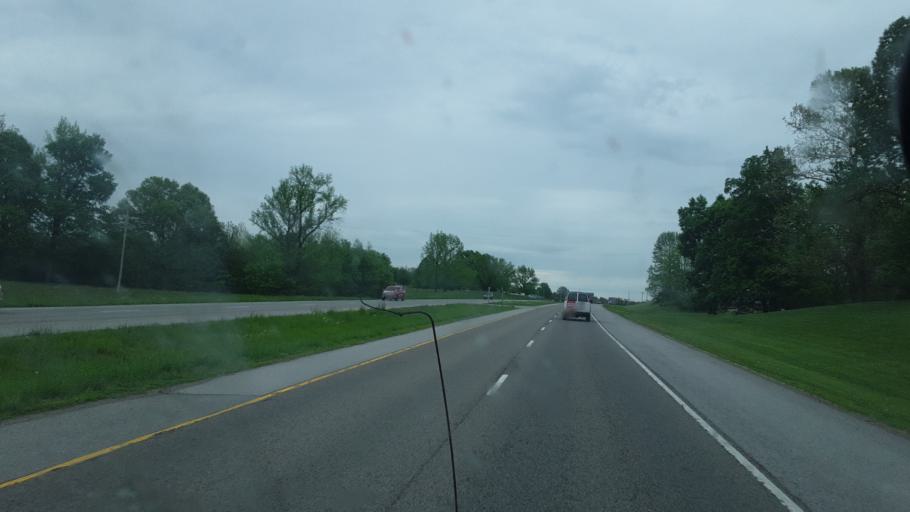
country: US
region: Illinois
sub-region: Jackson County
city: Murphysboro
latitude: 37.7635
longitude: -89.2870
